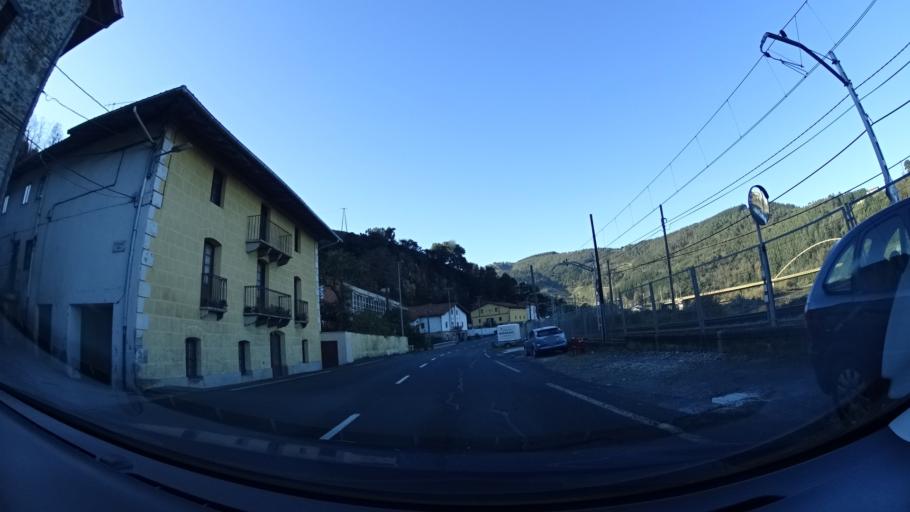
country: ES
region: Basque Country
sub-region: Provincia de Guipuzcoa
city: Deba
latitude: 43.2850
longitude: -2.3590
